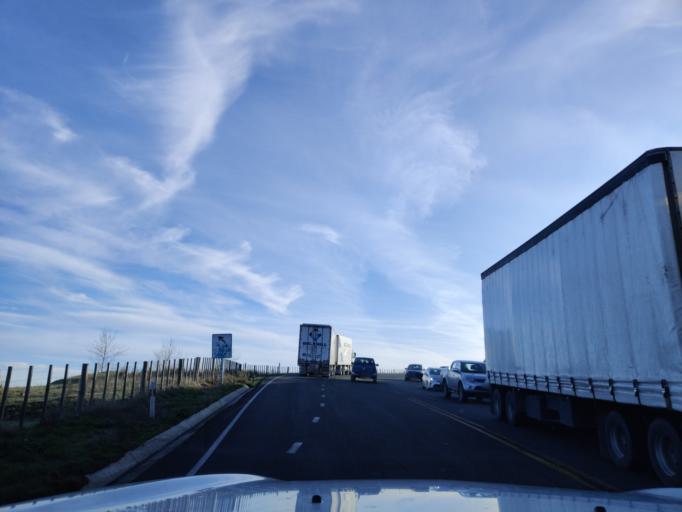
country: NZ
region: Manawatu-Wanganui
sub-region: Palmerston North City
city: Palmerston North
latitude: -40.2871
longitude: 175.7867
